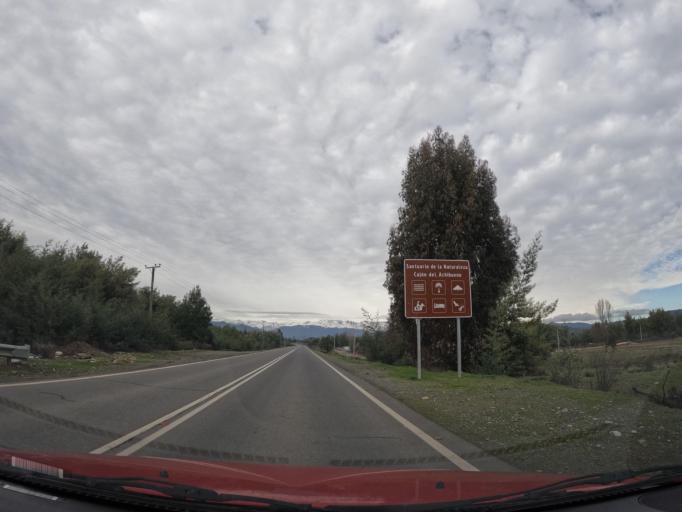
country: CL
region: Maule
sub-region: Provincia de Linares
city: Linares
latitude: -35.9072
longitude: -71.4973
